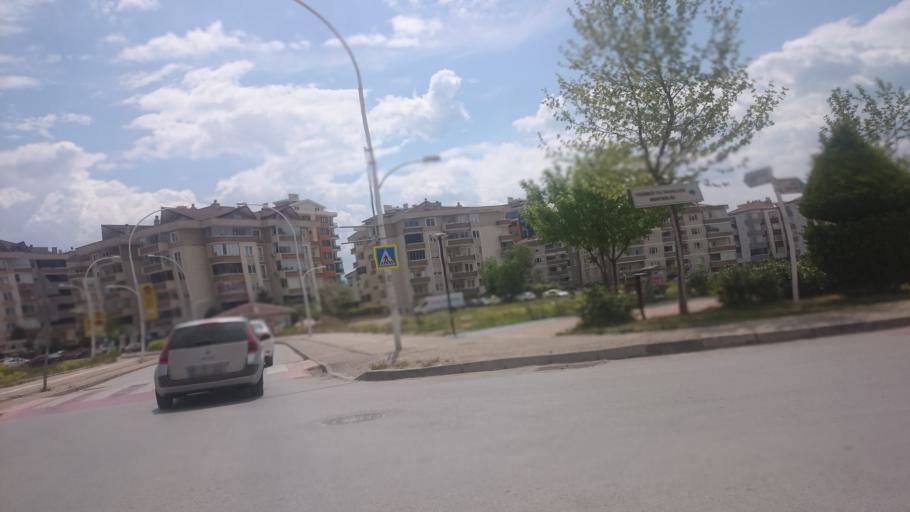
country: TR
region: Bursa
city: Cali
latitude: 40.2259
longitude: 28.9096
